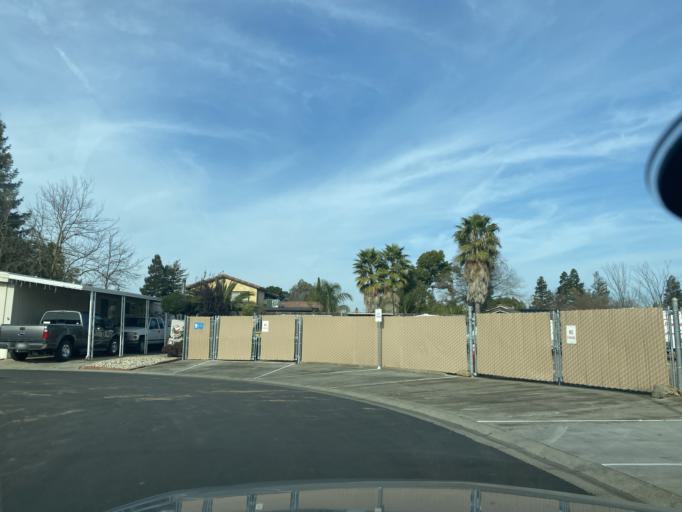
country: US
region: California
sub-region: Sacramento County
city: Elk Grove
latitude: 38.4048
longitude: -121.3824
